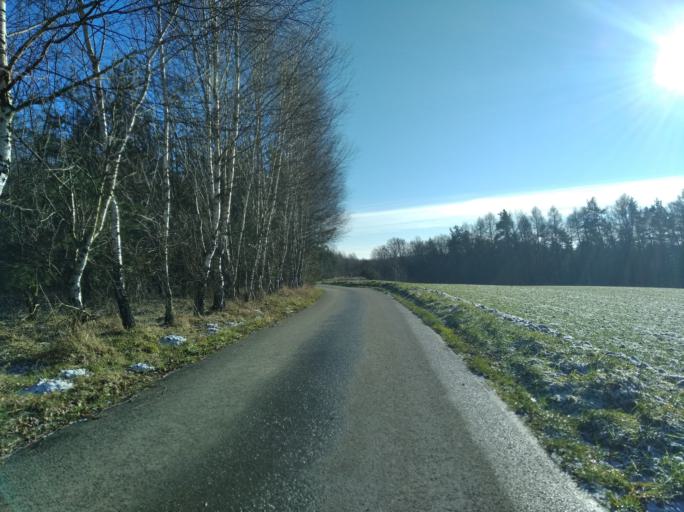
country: PL
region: Subcarpathian Voivodeship
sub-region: Powiat ropczycko-sedziszowski
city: Iwierzyce
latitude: 49.9605
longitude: 21.7517
